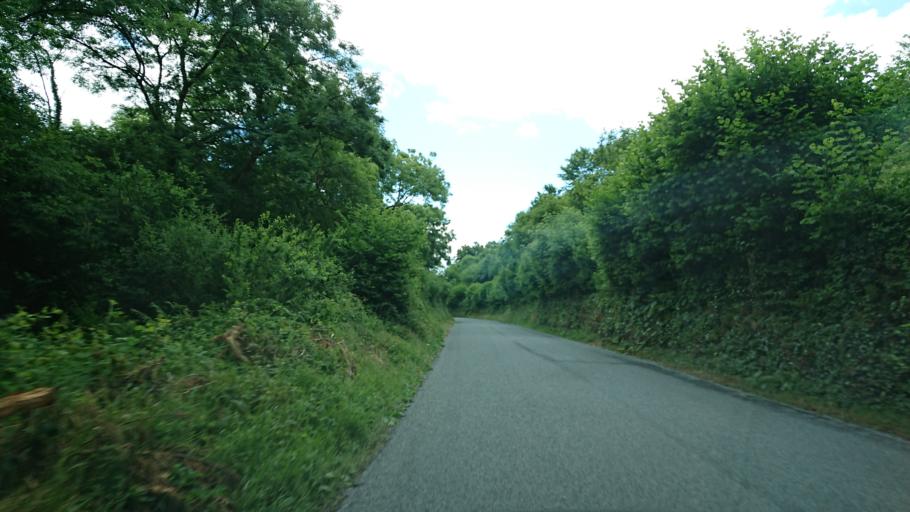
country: IE
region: Munster
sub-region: Waterford
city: Tra Mhor
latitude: 52.1778
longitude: -7.1498
